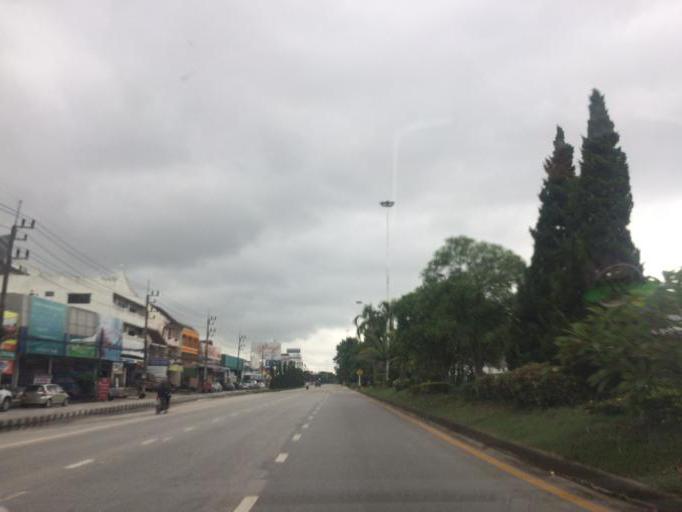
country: TH
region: Chiang Rai
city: Chiang Rai
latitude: 19.8990
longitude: 99.8392
